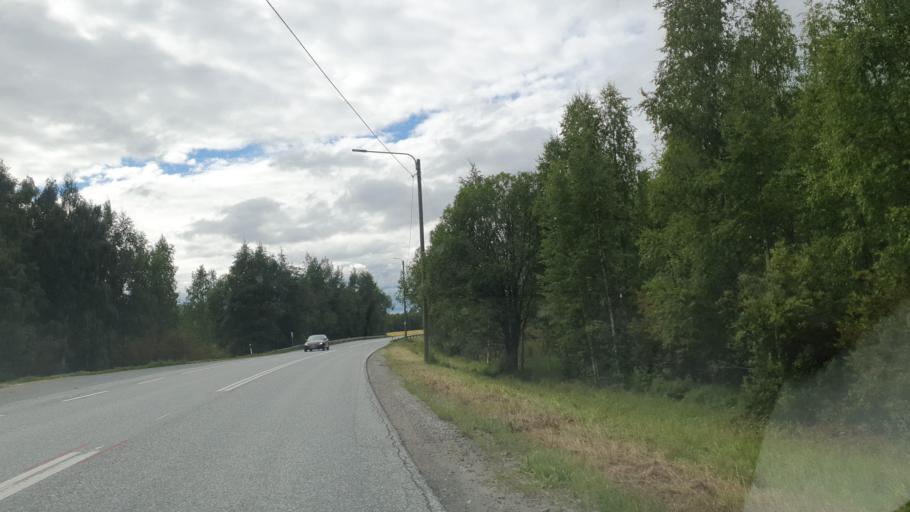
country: FI
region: Northern Savo
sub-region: Ylae-Savo
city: Iisalmi
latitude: 63.5183
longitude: 27.2319
